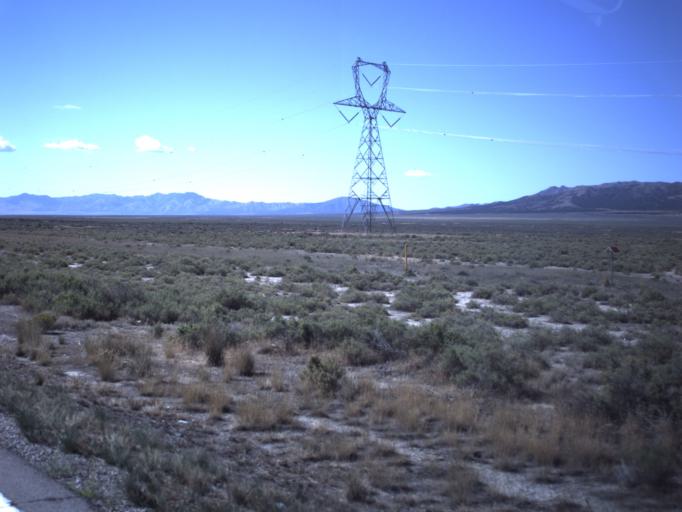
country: US
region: Utah
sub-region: Tooele County
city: Tooele
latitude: 40.2923
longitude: -112.4010
